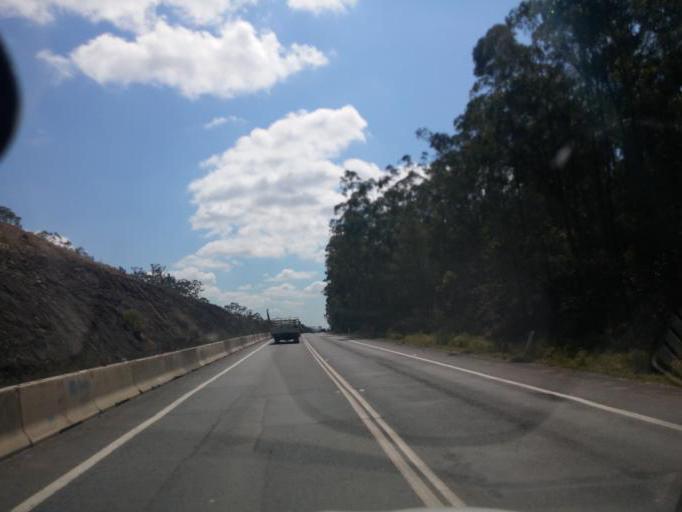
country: AU
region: New South Wales
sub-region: Port Macquarie-Hastings
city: North Shore
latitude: -31.2684
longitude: 152.8128
